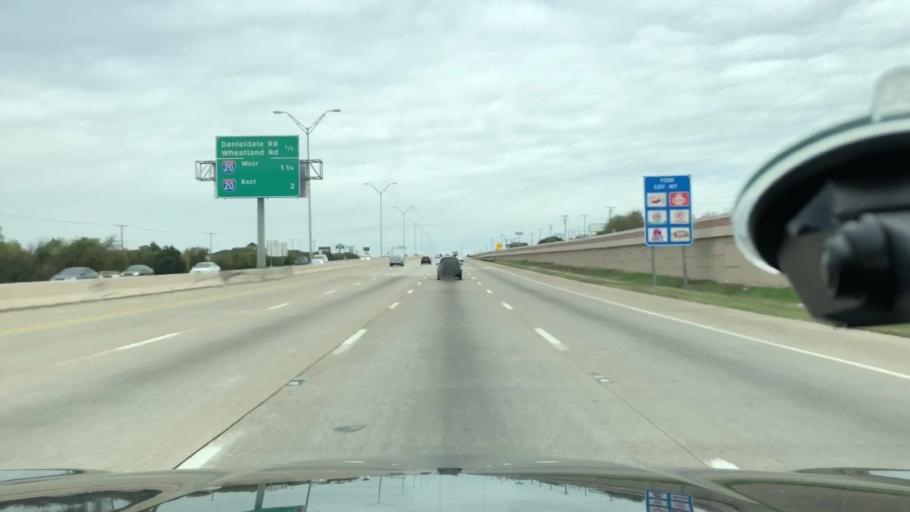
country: US
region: Texas
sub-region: Dallas County
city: DeSoto
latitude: 32.6122
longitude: -96.8229
